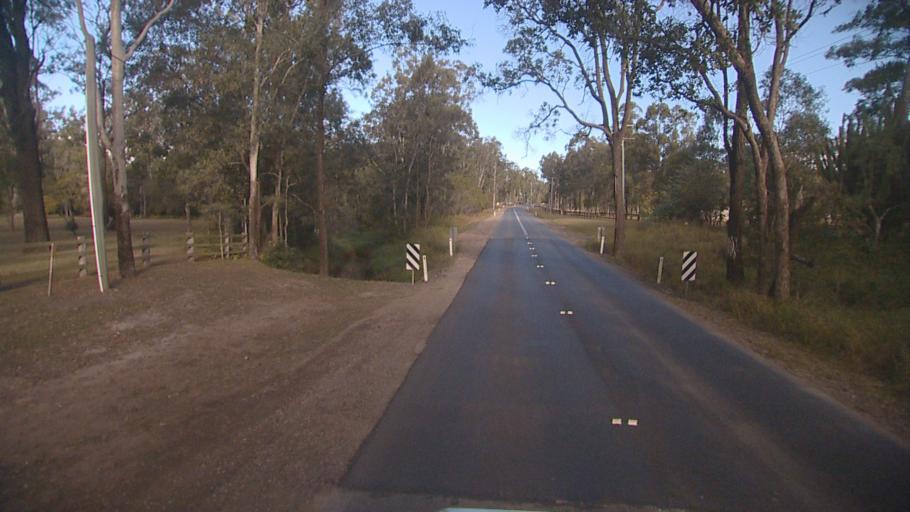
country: AU
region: Queensland
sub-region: Logan
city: Cedar Vale
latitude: -27.8492
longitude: 153.0512
